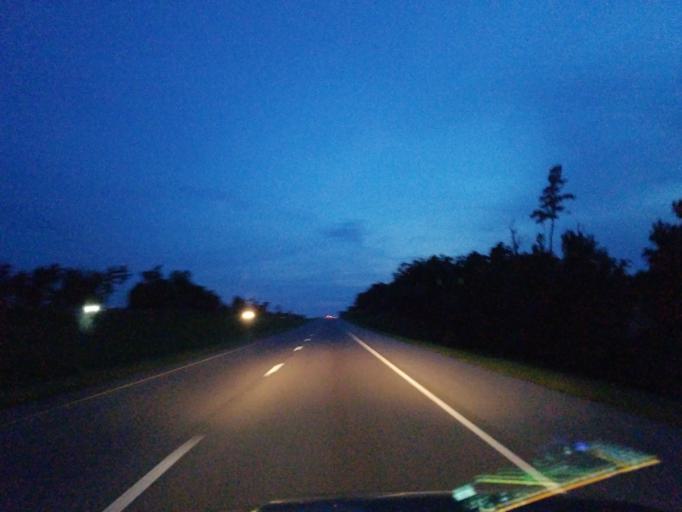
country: US
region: Mississippi
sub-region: Jones County
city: Ellisville
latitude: 31.5620
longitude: -89.2563
